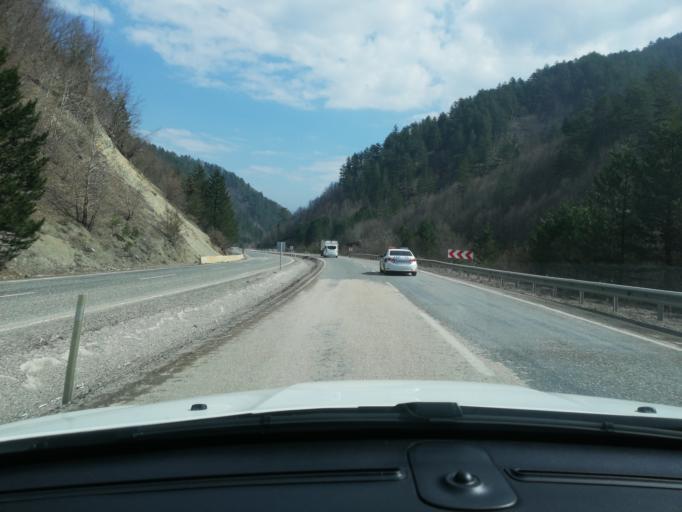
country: TR
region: Kastamonu
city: Kuzyaka
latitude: 41.1243
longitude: 33.7650
